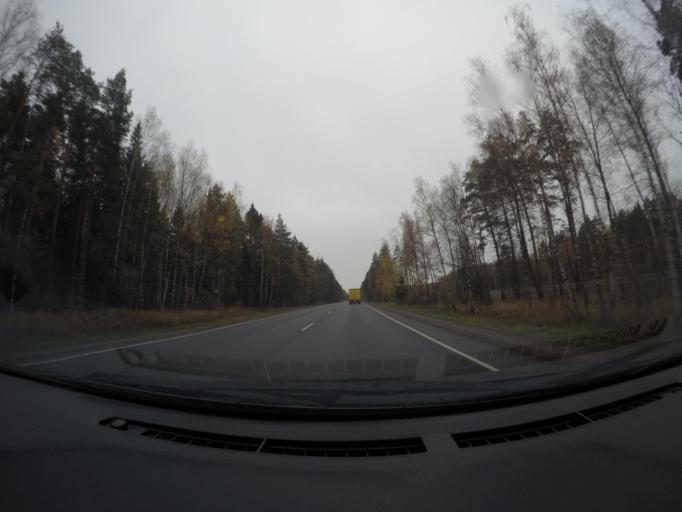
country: RU
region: Moskovskaya
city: Gzhel'
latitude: 55.5642
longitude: 38.3948
